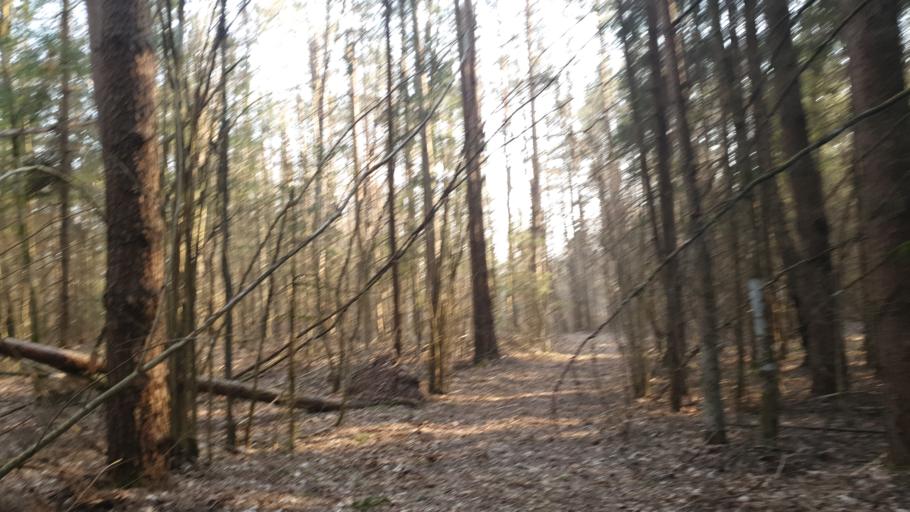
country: LT
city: Nemencine
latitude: 54.8736
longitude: 25.5713
